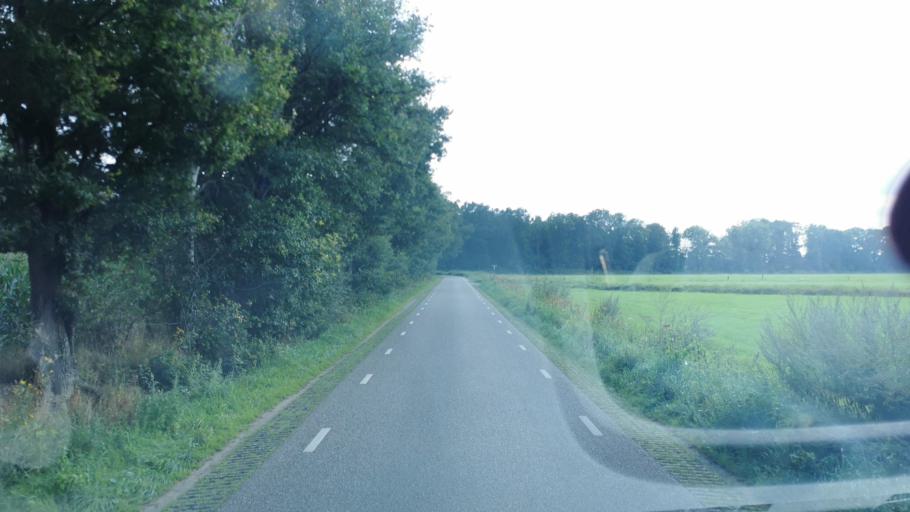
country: NL
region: Overijssel
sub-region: Gemeente Hengelo
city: Hengelo
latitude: 52.3215
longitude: 6.8282
